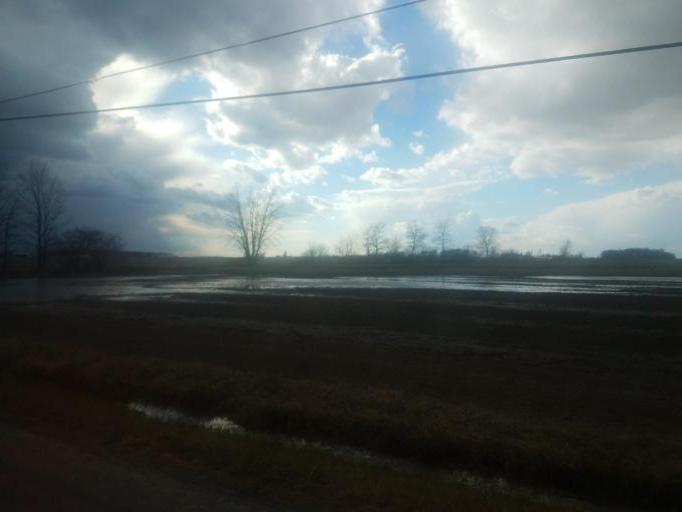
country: US
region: Ohio
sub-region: Marion County
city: Prospect
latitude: 40.4616
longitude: -83.1116
